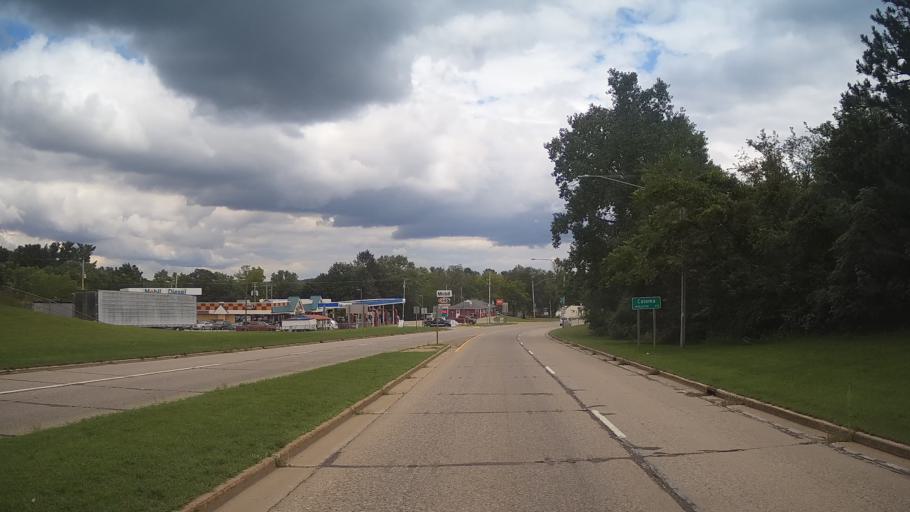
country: US
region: Wisconsin
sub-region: Marquette County
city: Westfield
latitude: 44.0355
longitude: -89.5263
